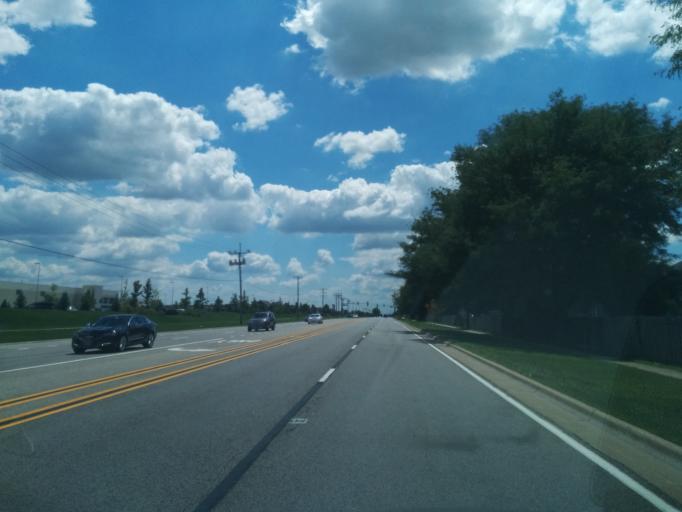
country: US
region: Illinois
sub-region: Will County
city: Romeoville
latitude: 41.6781
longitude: -88.1257
